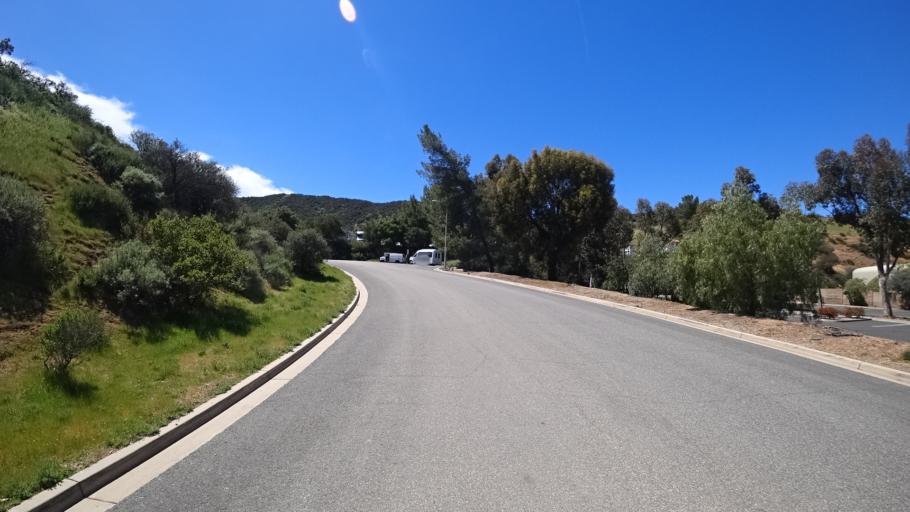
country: US
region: California
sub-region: Ventura County
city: Thousand Oaks
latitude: 34.1686
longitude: -118.8487
